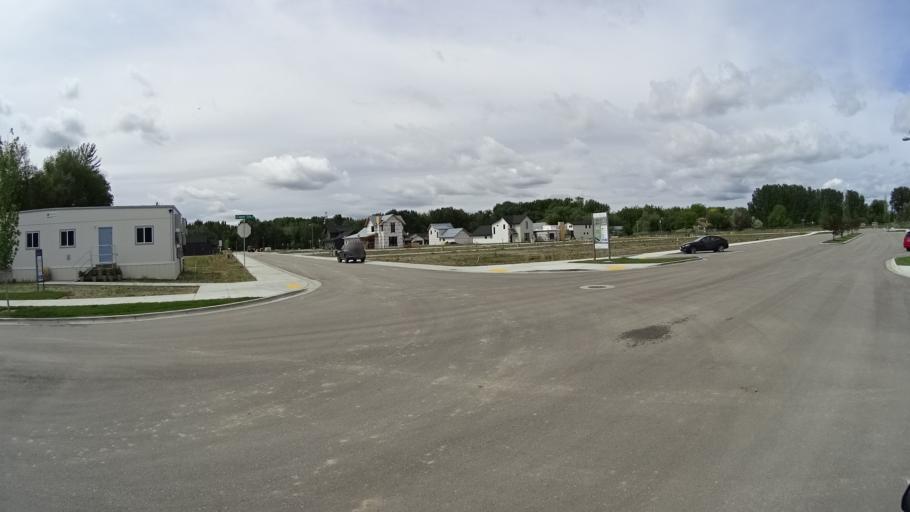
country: US
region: Idaho
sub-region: Ada County
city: Eagle
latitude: 43.6944
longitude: -116.3846
